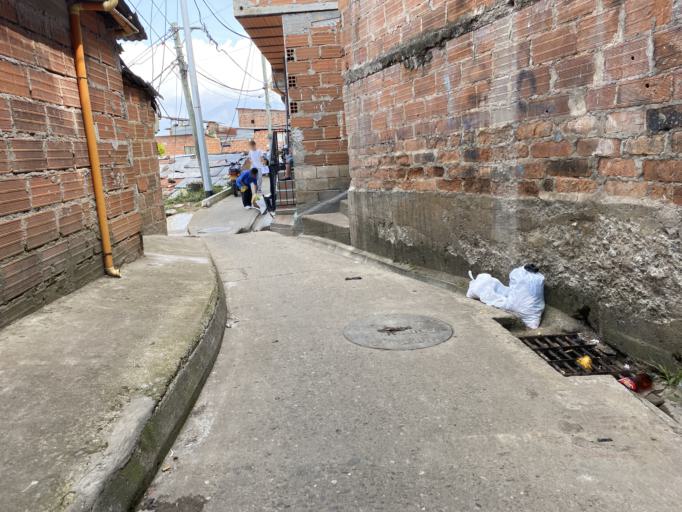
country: CO
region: Antioquia
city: Medellin
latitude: 6.2785
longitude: -75.5444
